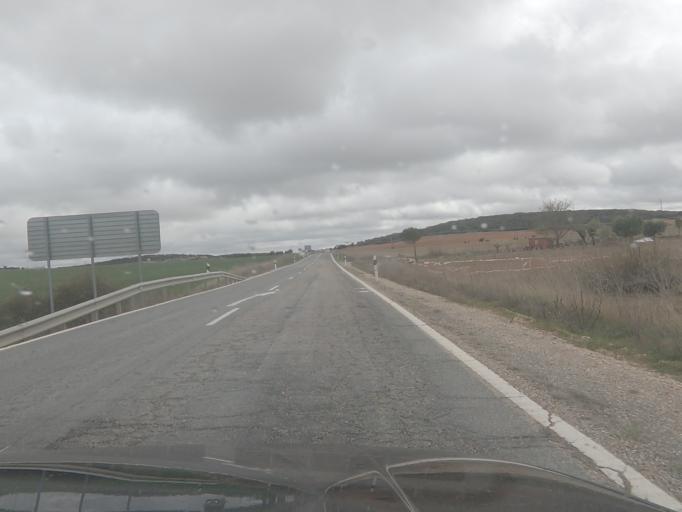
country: ES
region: Castille and Leon
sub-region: Provincia de Zamora
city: Montamarta
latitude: 41.6944
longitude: -5.8128
